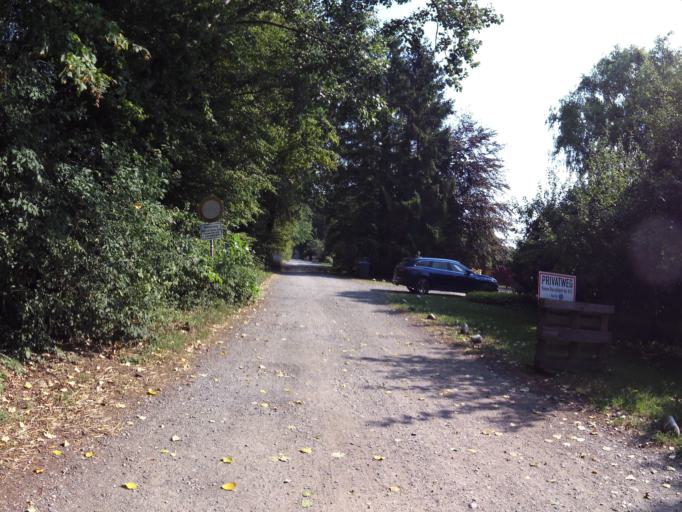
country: DE
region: North Rhine-Westphalia
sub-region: Regierungsbezirk Munster
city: Altenberge
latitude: 51.9724
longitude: 7.5092
